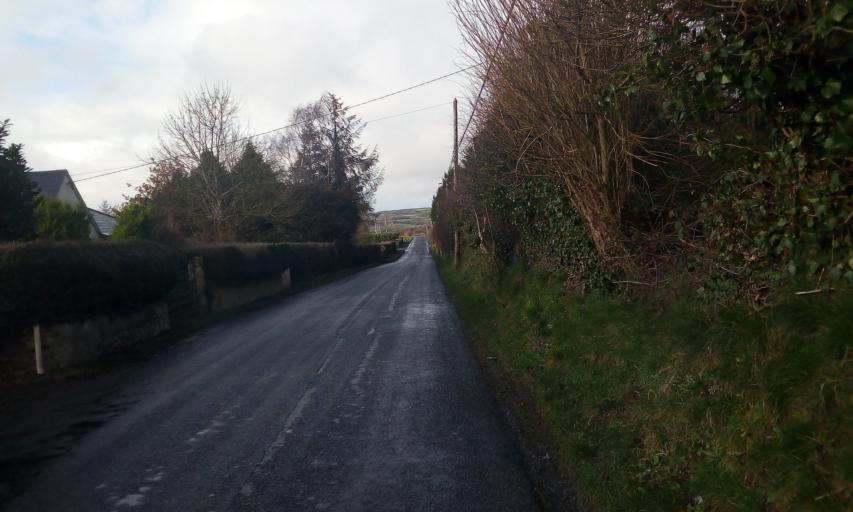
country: IE
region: Leinster
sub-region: Kilkenny
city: Castlecomer
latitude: 52.8013
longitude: -7.1915
